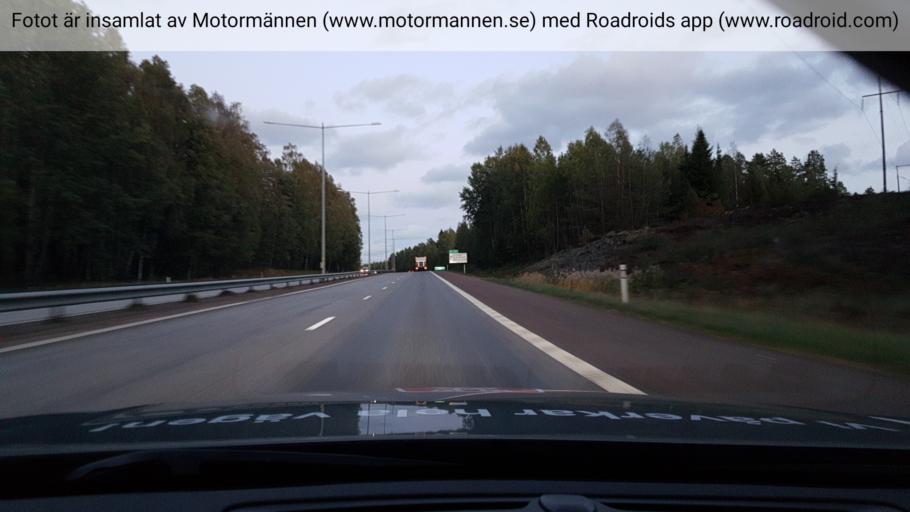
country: SE
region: Vaermland
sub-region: Karlstads Kommun
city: Karlstad
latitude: 59.3997
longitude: 13.5619
